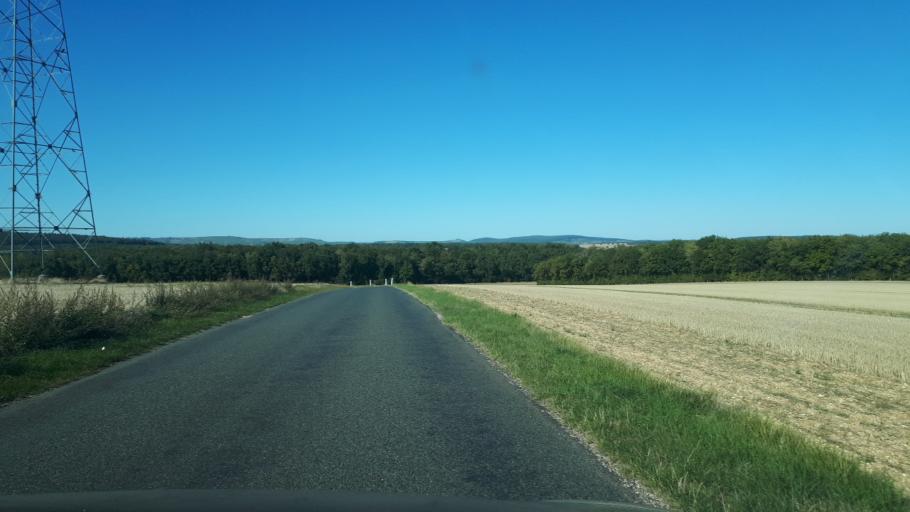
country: FR
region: Centre
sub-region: Departement du Cher
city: Sancerre
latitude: 47.2214
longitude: 2.7531
